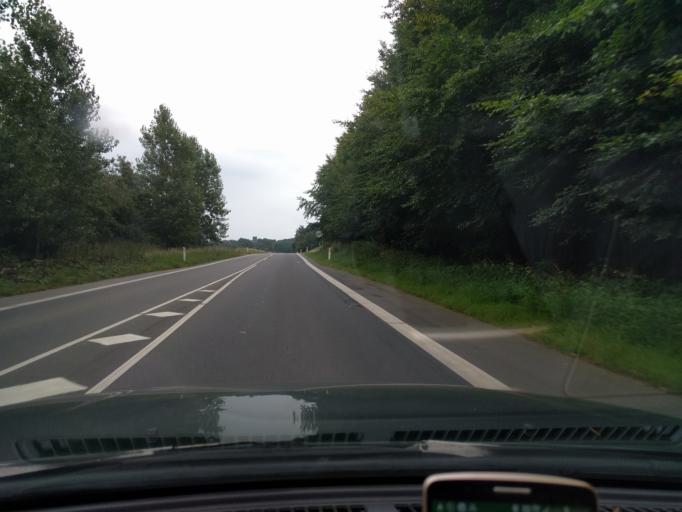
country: DK
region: Zealand
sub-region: Naestved Kommune
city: Fuglebjerg
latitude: 55.2333
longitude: 11.4697
